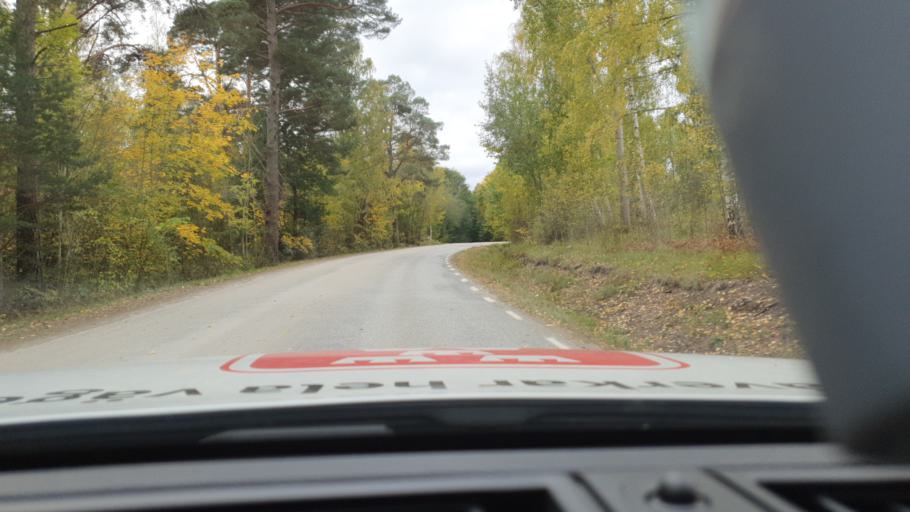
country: SE
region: Stockholm
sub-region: Upplands-Bro Kommun
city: Bro
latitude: 59.4937
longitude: 17.5699
